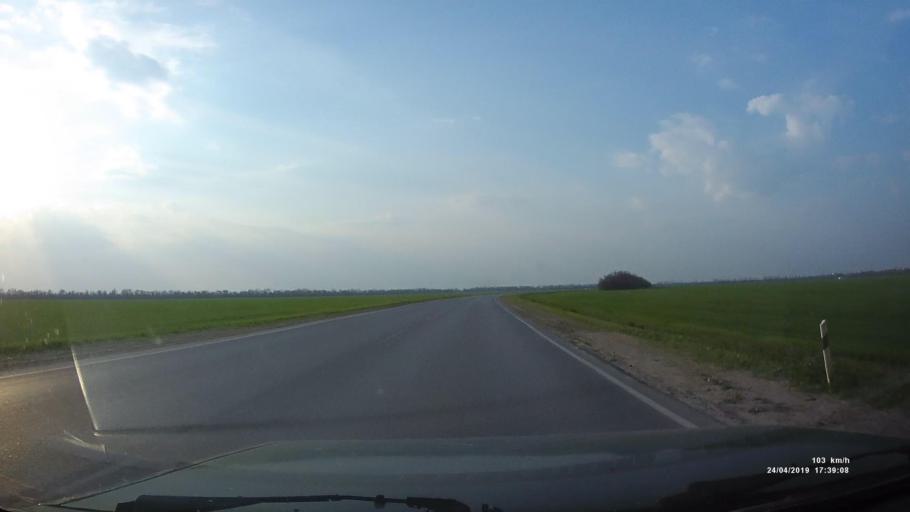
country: RU
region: Rostov
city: Tselina
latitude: 46.5188
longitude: 40.9939
